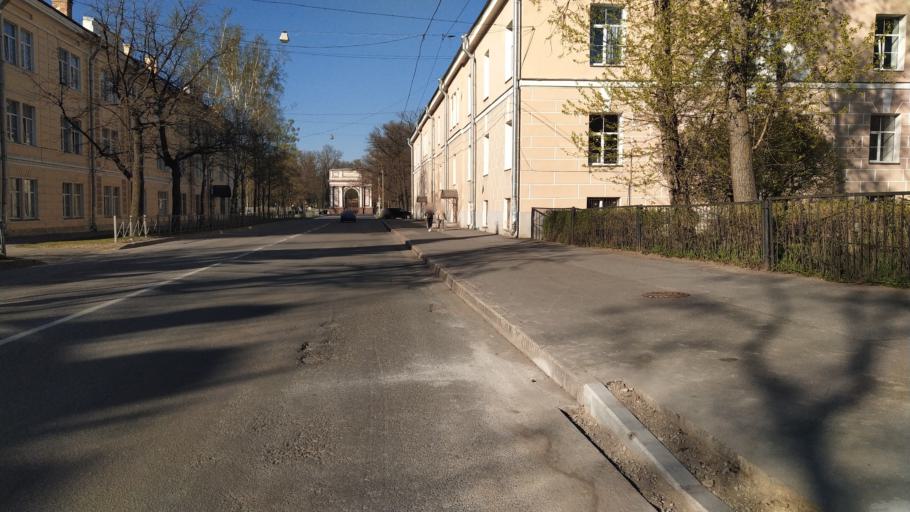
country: RU
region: St.-Petersburg
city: Pushkin
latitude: 59.7079
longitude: 30.3801
